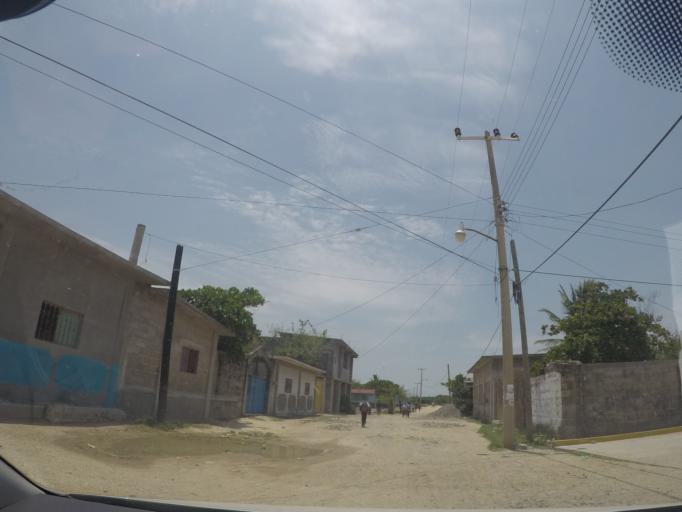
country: MX
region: Oaxaca
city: San Mateo del Mar
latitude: 16.2117
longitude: -94.9818
